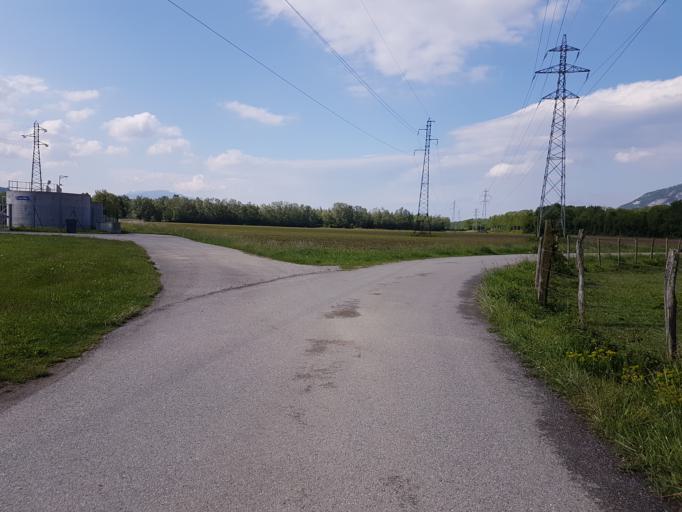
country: FR
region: Rhone-Alpes
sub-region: Departement de la Savoie
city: Chindrieux
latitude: 45.8856
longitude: 5.8396
